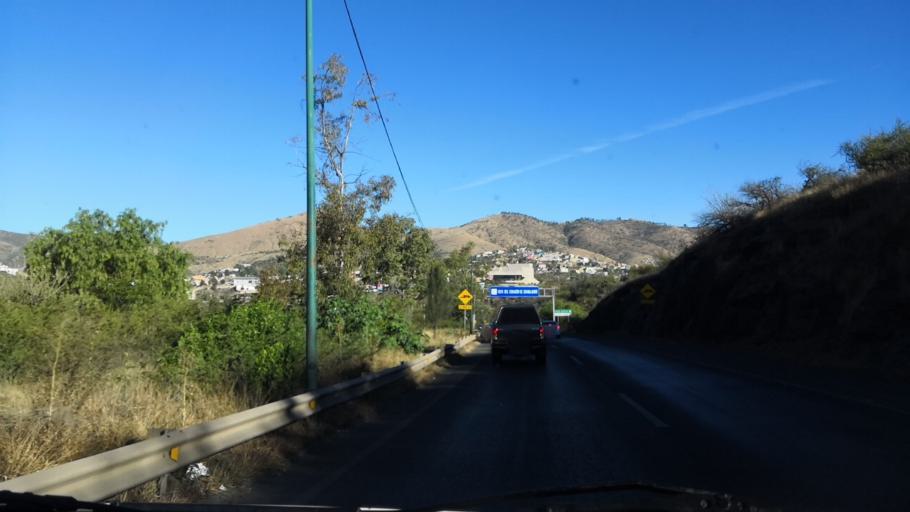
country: MX
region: Guanajuato
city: Marfil
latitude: 21.0047
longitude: -101.2709
